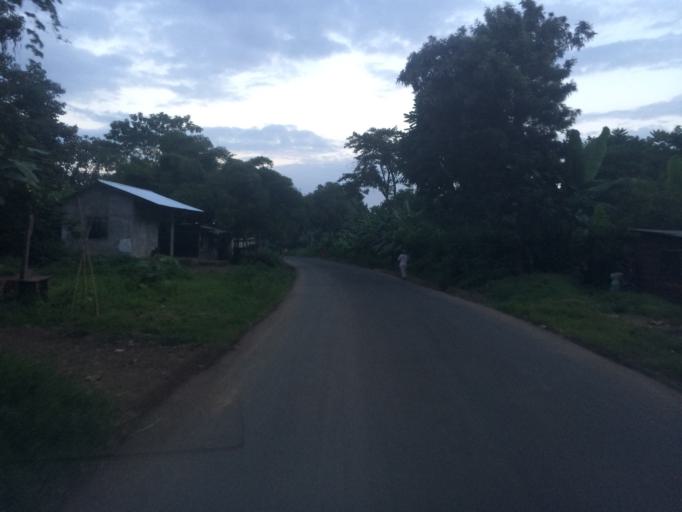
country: TZ
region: Arusha
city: Usa River
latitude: -3.3684
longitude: 36.8165
